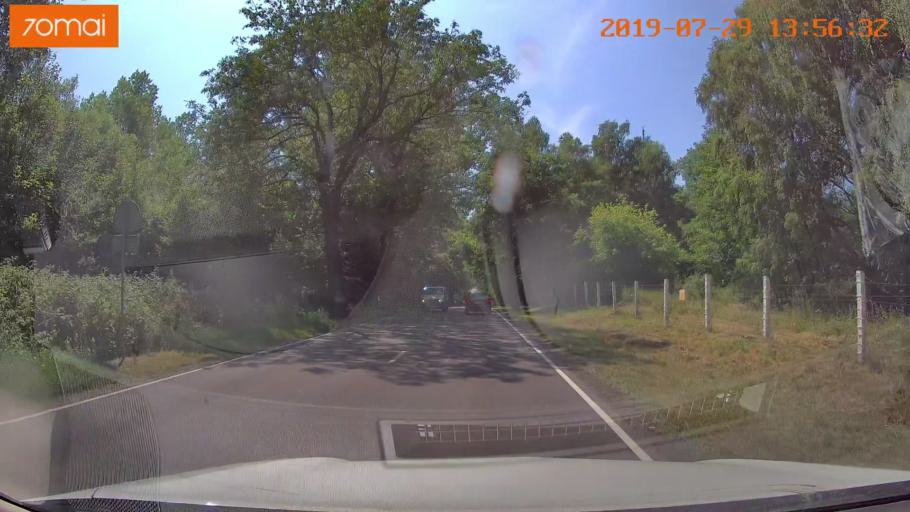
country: RU
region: Kaliningrad
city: Primorsk
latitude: 54.7075
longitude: 19.9484
